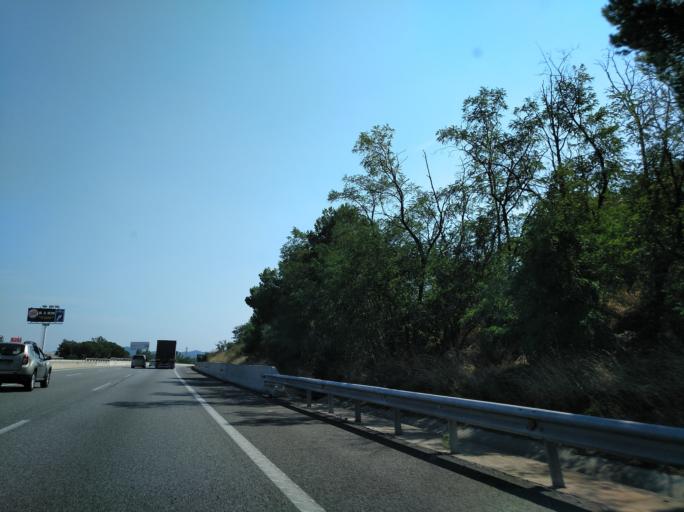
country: ES
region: Catalonia
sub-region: Provincia de Girona
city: Sils
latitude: 41.8104
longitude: 2.7485
